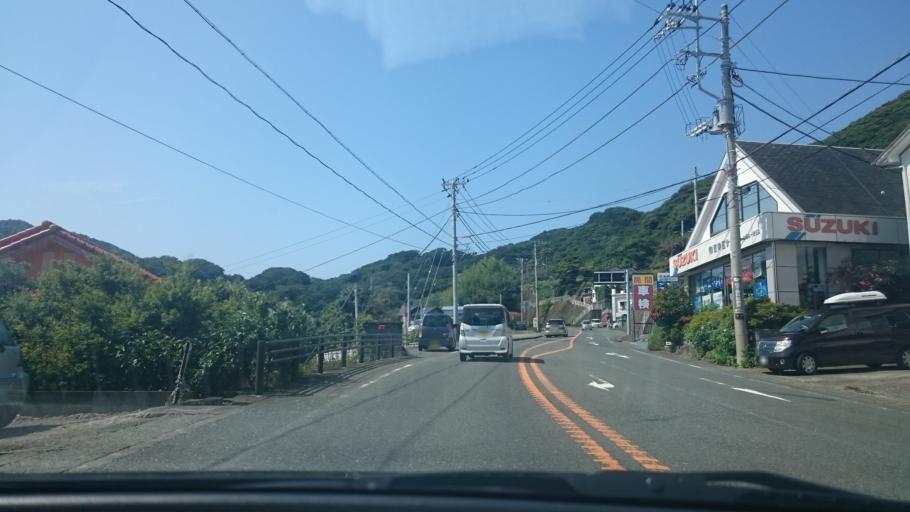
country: JP
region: Shizuoka
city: Heda
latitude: 34.8110
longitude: 138.7729
